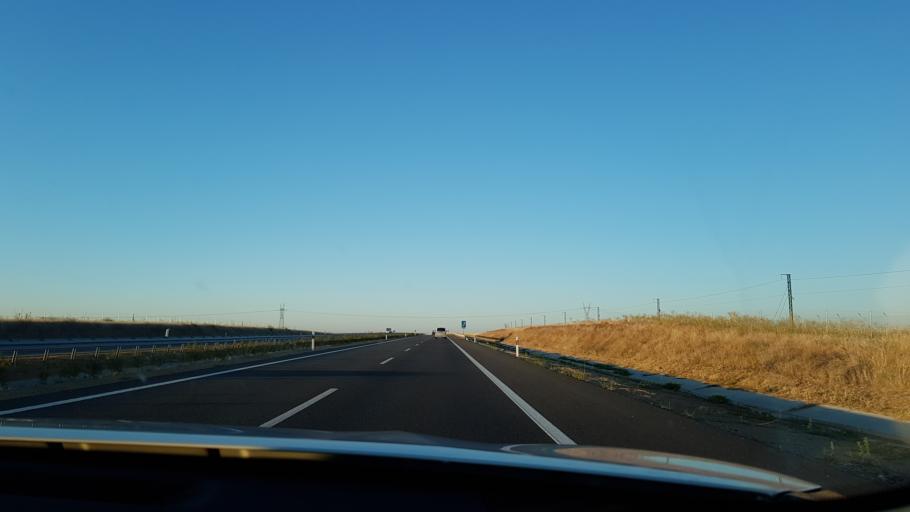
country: ES
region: Castille and Leon
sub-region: Provincia de Zamora
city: Montamarta
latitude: 41.6183
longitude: -5.7878
